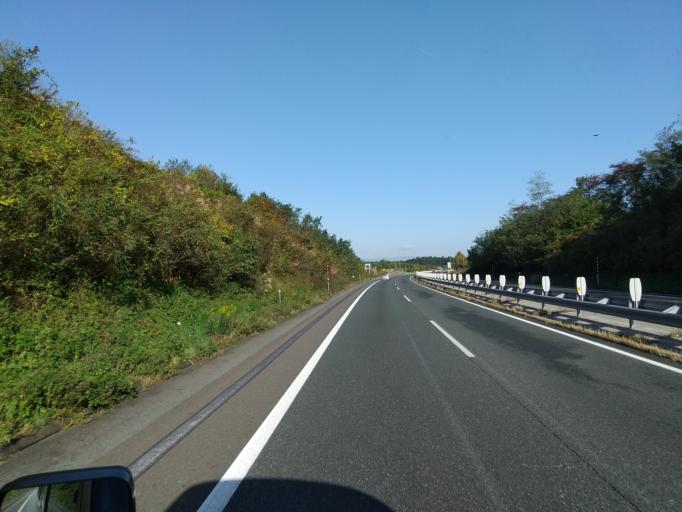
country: JP
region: Iwate
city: Mizusawa
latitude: 39.0682
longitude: 141.1013
